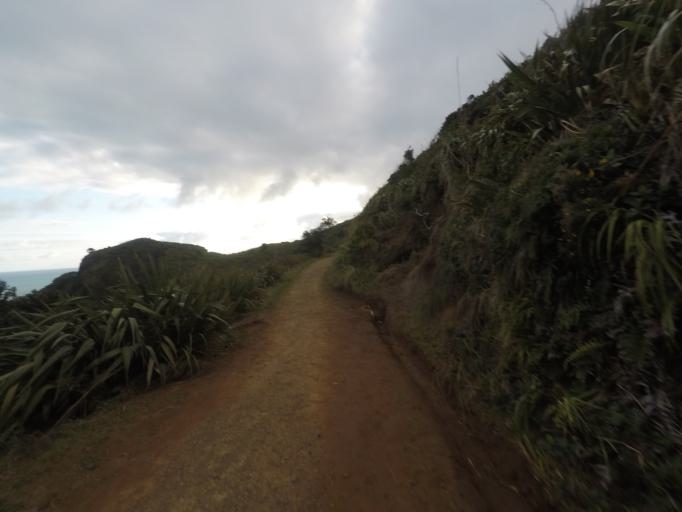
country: NZ
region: Auckland
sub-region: Auckland
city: Muriwai Beach
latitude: -36.9740
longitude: 174.4707
